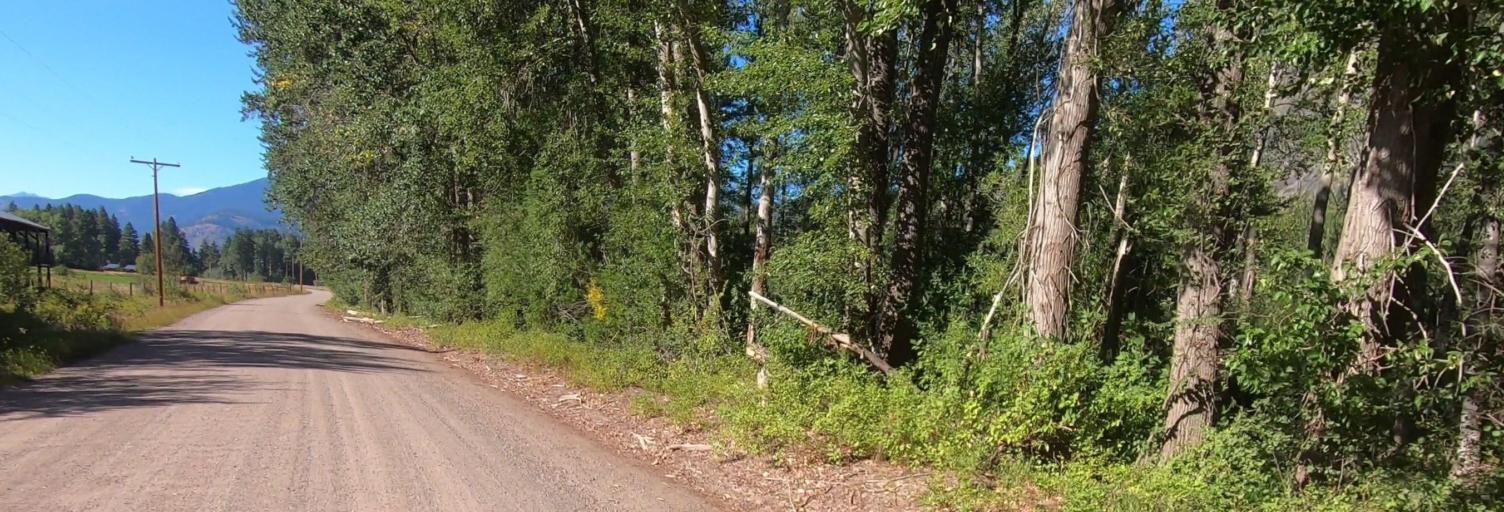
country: US
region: Washington
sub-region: Chelan County
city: Granite Falls
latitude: 48.5352
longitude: -120.3263
